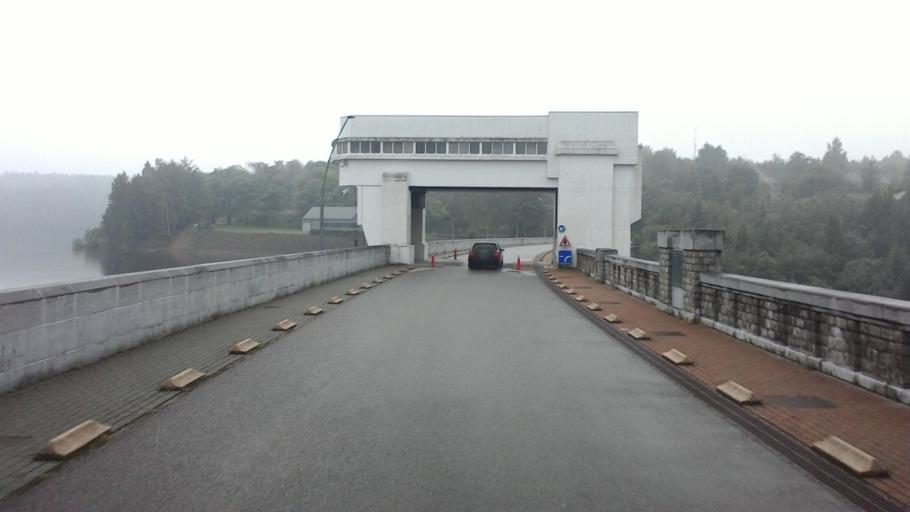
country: BE
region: Wallonia
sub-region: Province de Liege
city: Eupen
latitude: 50.6183
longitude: 6.0904
